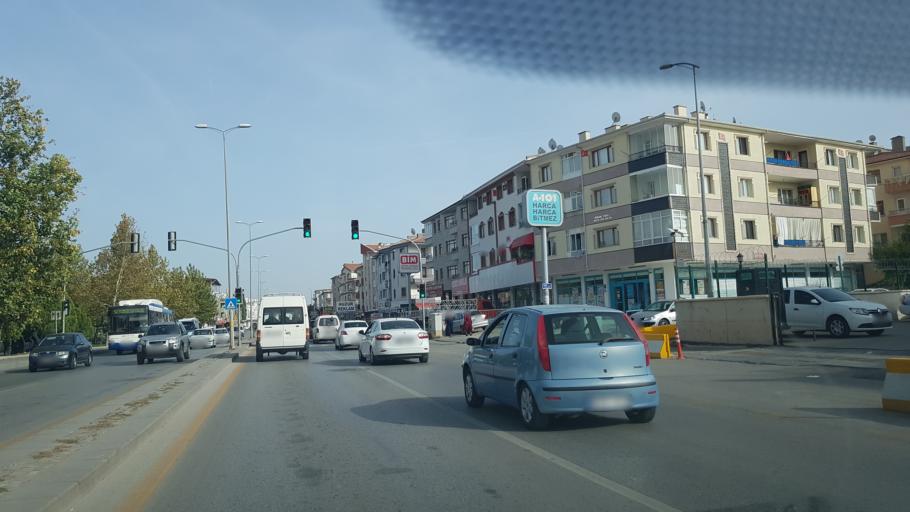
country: TR
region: Ankara
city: Etimesgut
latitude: 39.9550
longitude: 32.6306
